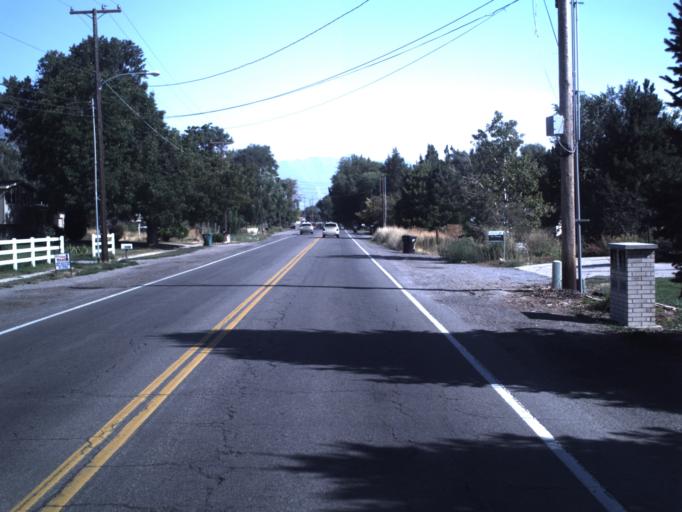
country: US
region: Utah
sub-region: Utah County
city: Provo
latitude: 40.2490
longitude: -111.7023
